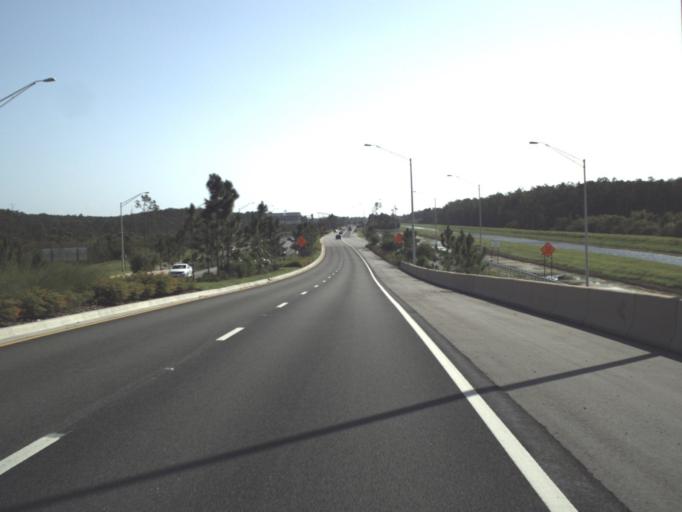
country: US
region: Florida
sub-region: Lee County
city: Three Oaks
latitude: 26.5118
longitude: -81.7841
